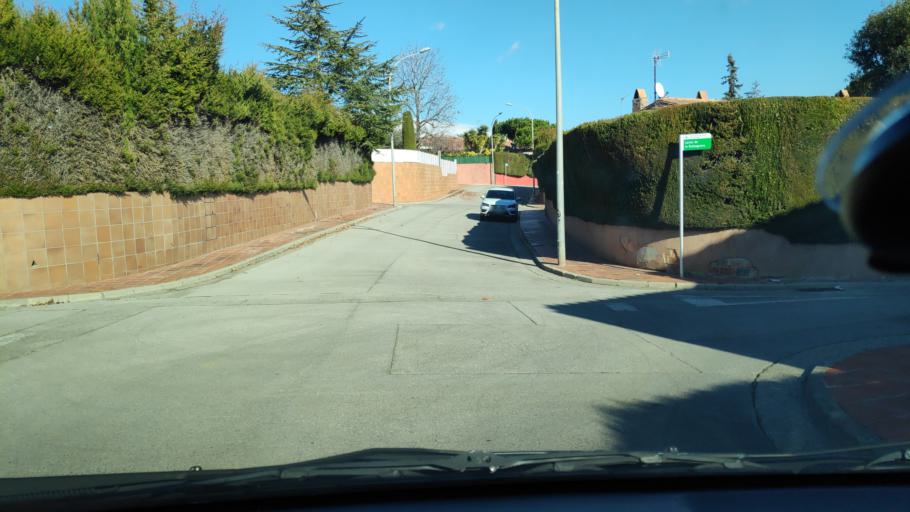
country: ES
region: Catalonia
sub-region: Provincia de Barcelona
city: Sant Quirze del Valles
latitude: 41.5263
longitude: 2.0734
